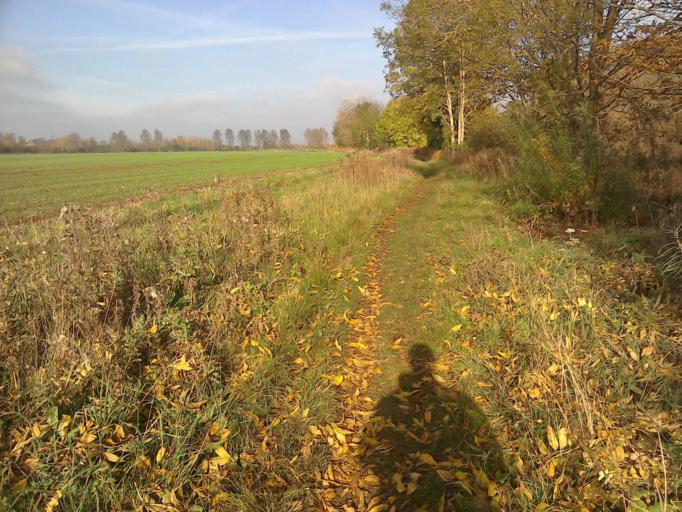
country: GB
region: England
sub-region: Oxfordshire
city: Radley
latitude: 51.6801
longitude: -1.2254
